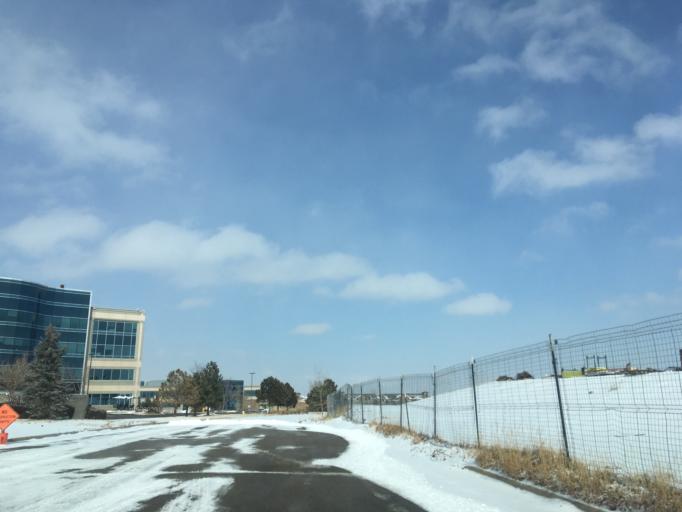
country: US
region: Colorado
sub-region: Broomfield County
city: Broomfield
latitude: 39.9125
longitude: -105.1061
